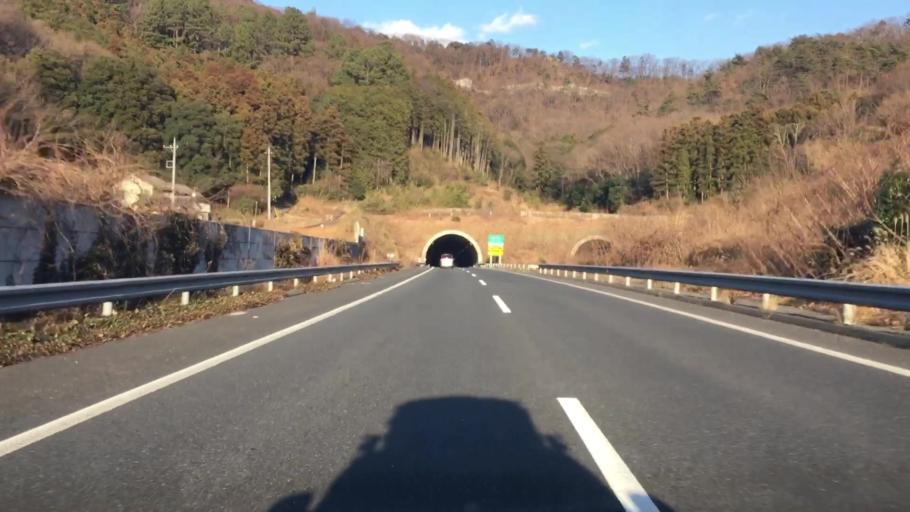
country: JP
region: Tochigi
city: Ashikaga
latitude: 36.3619
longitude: 139.4416
